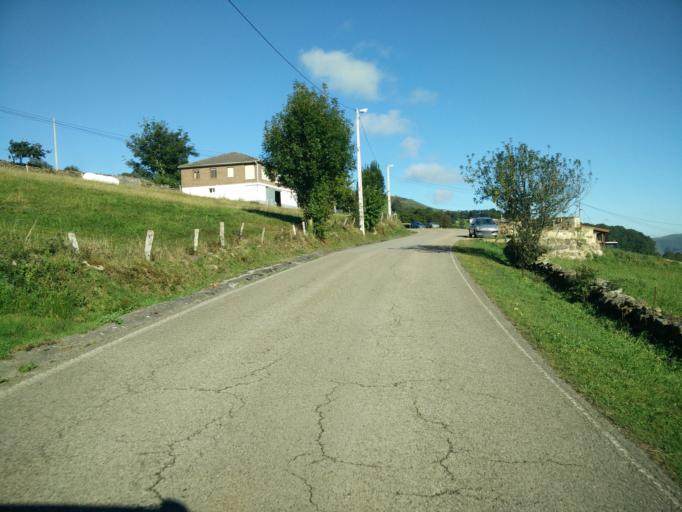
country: ES
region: Cantabria
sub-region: Provincia de Cantabria
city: San Pedro del Romeral
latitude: 43.1104
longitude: -3.8097
